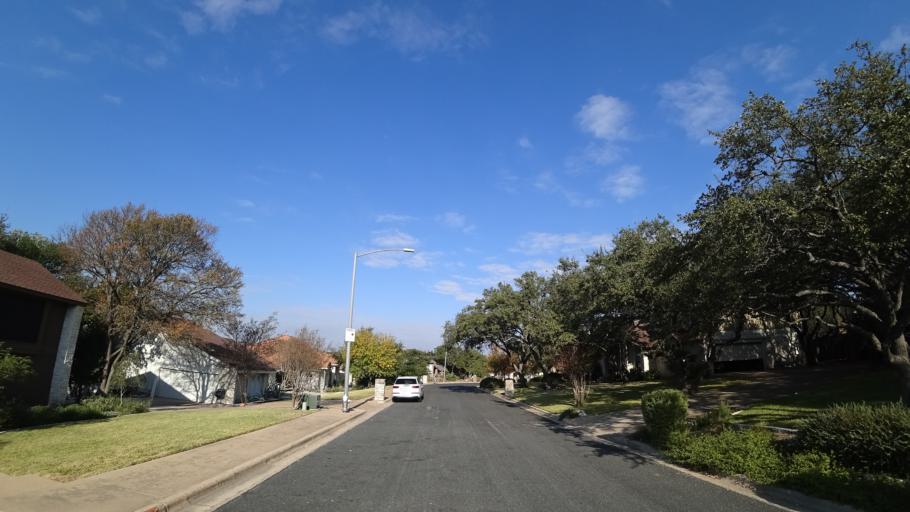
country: US
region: Texas
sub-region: Williamson County
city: Jollyville
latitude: 30.3971
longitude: -97.7604
